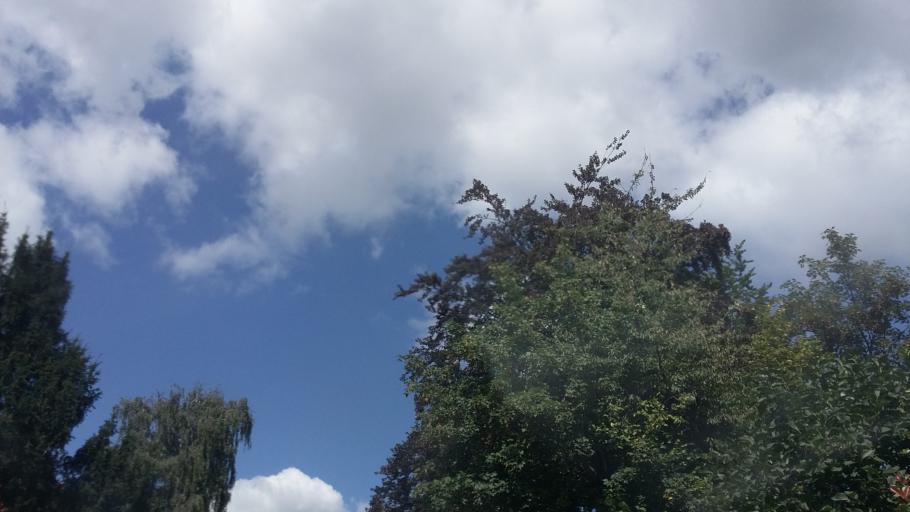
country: DE
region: Bavaria
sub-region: Upper Bavaria
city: Germering
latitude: 48.1269
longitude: 11.3717
